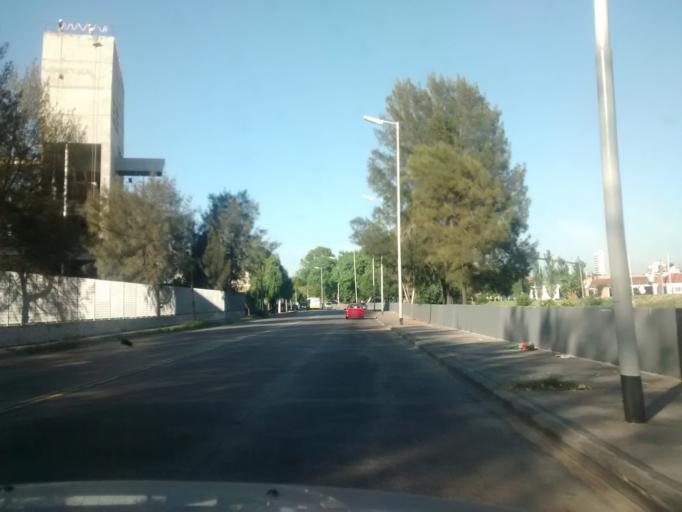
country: AR
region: Buenos Aires
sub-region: Partido de Avellaneda
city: Avellaneda
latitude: -34.6781
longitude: -58.3369
